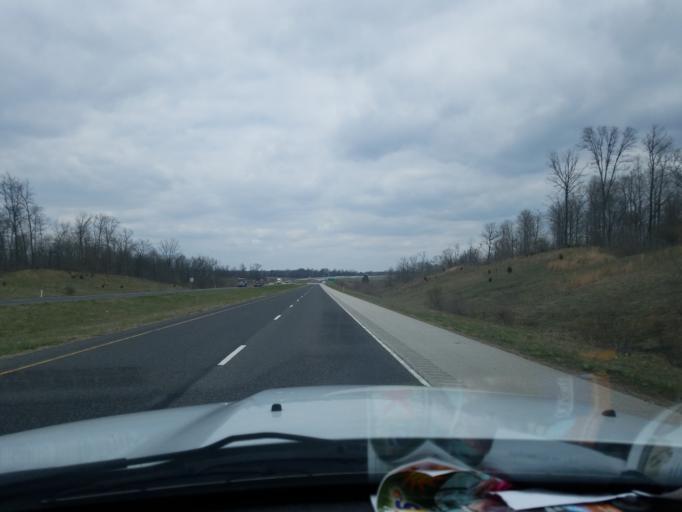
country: US
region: Indiana
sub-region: Vigo County
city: Terre Haute
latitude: 39.3875
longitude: -87.3729
